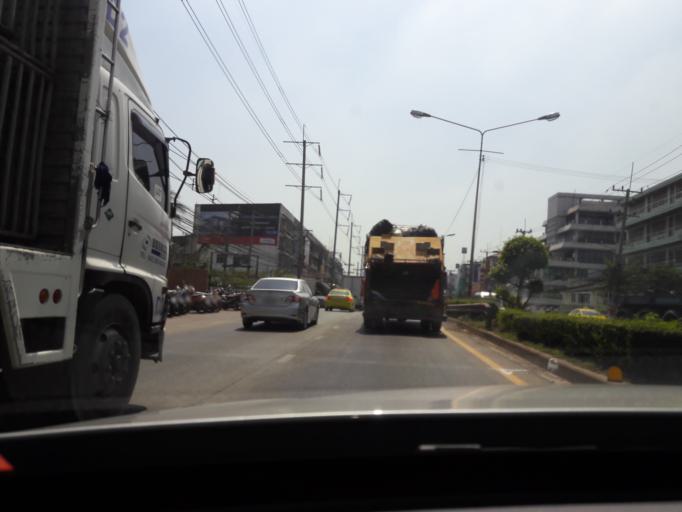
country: TH
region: Samut Sakhon
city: Samut Sakhon
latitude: 13.5703
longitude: 100.2721
